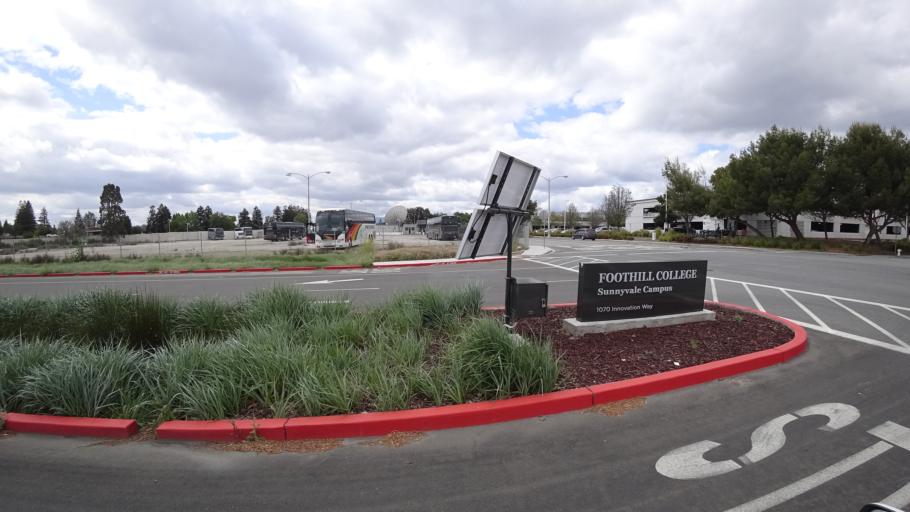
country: US
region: California
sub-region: Santa Clara County
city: Sunnyvale
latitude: 37.4044
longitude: -122.0295
